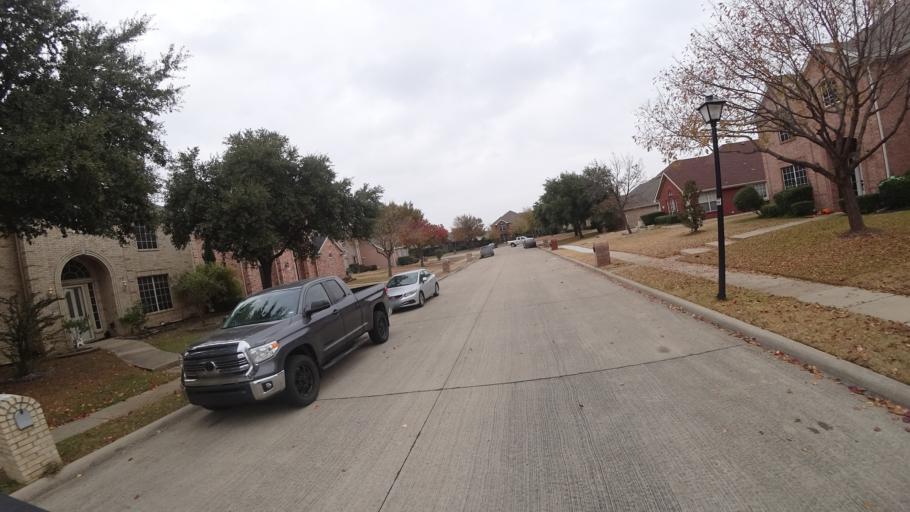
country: US
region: Texas
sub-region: Denton County
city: Lewisville
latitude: 33.0189
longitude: -96.9380
